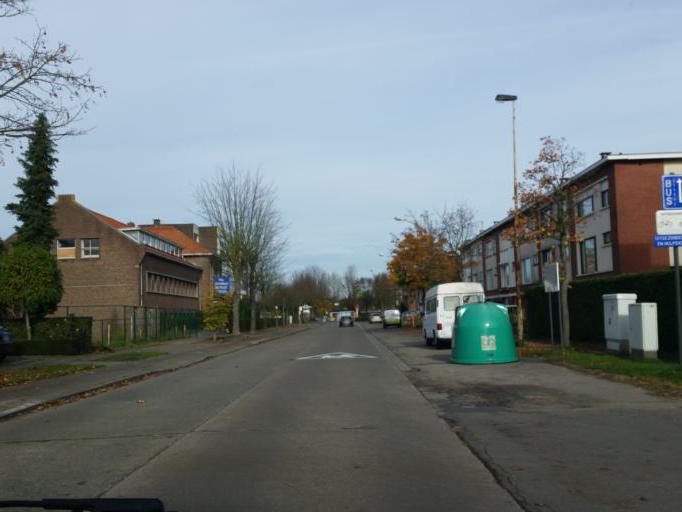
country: BE
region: Flanders
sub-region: Provincie Antwerpen
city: Kontich
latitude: 51.1414
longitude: 4.4471
